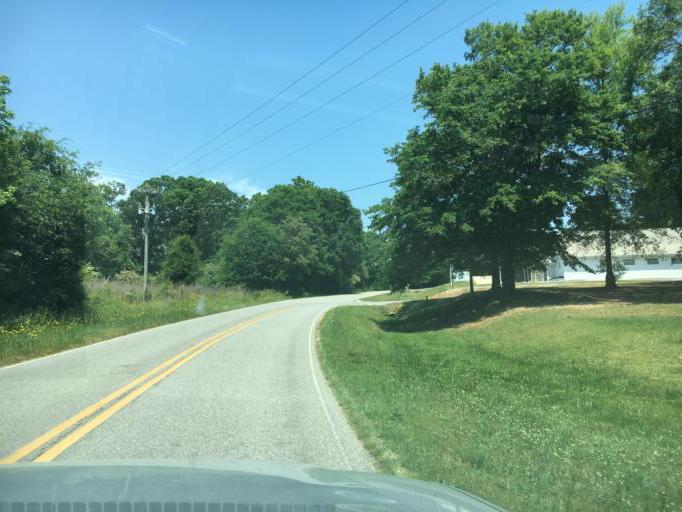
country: US
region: Georgia
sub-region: Hart County
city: Royston
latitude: 34.2925
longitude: -83.0865
